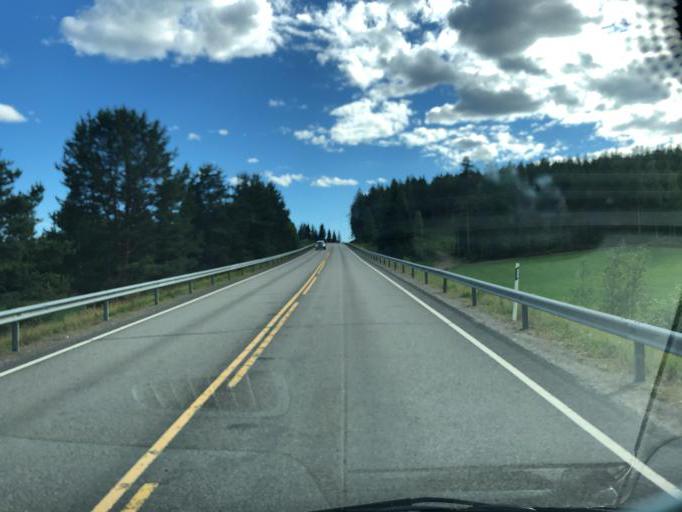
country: FI
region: Kymenlaakso
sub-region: Kouvola
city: Kouvola
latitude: 60.9789
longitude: 26.9073
